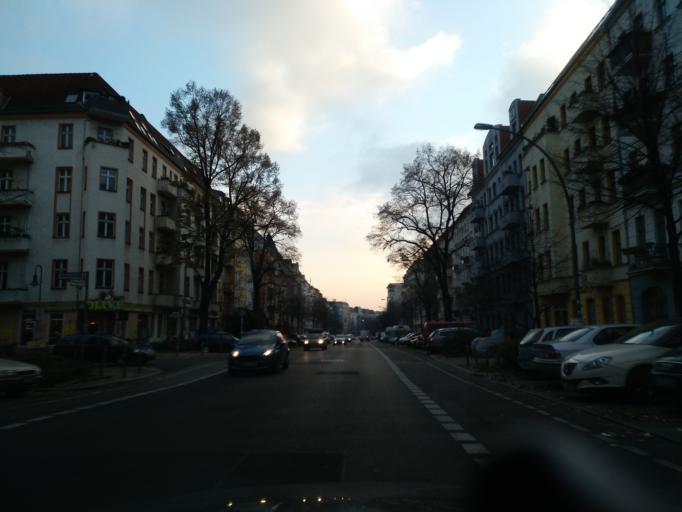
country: DE
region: Berlin
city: Friedrichshain Bezirk
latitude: 52.5183
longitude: 13.4617
